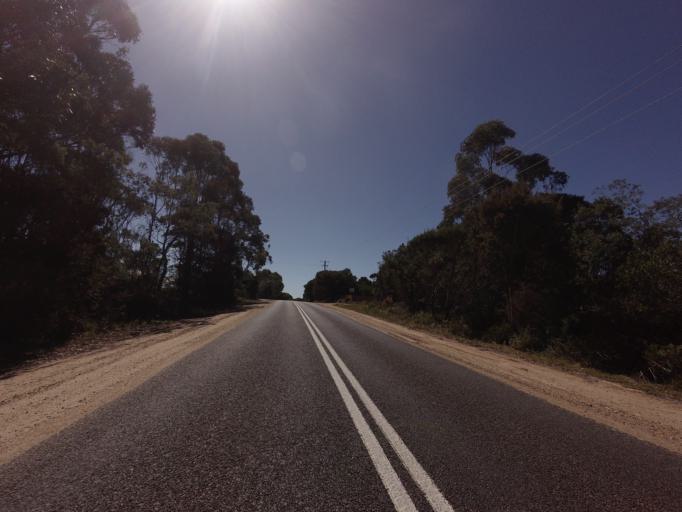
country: AU
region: Tasmania
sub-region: Break O'Day
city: St Helens
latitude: -41.8287
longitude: 148.2610
